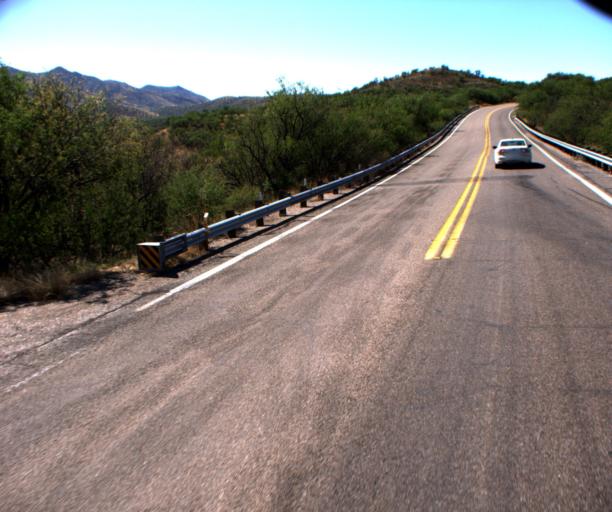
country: US
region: Arizona
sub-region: Santa Cruz County
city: Rio Rico
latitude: 31.4968
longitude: -110.8112
